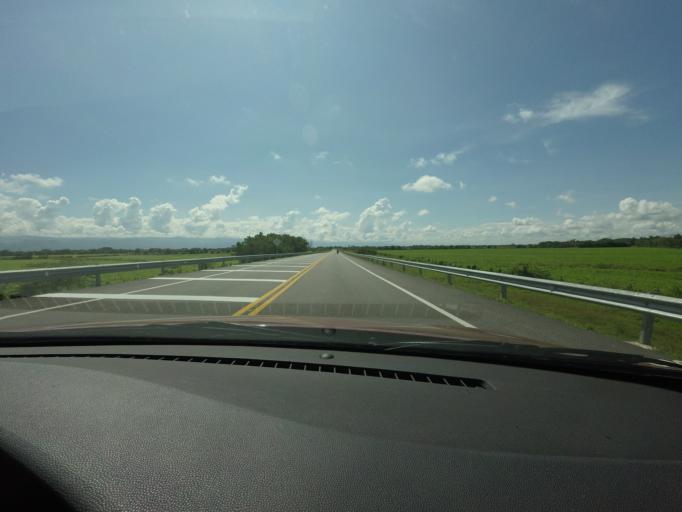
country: CO
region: Tolima
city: Espinal
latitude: 4.1454
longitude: -74.9117
